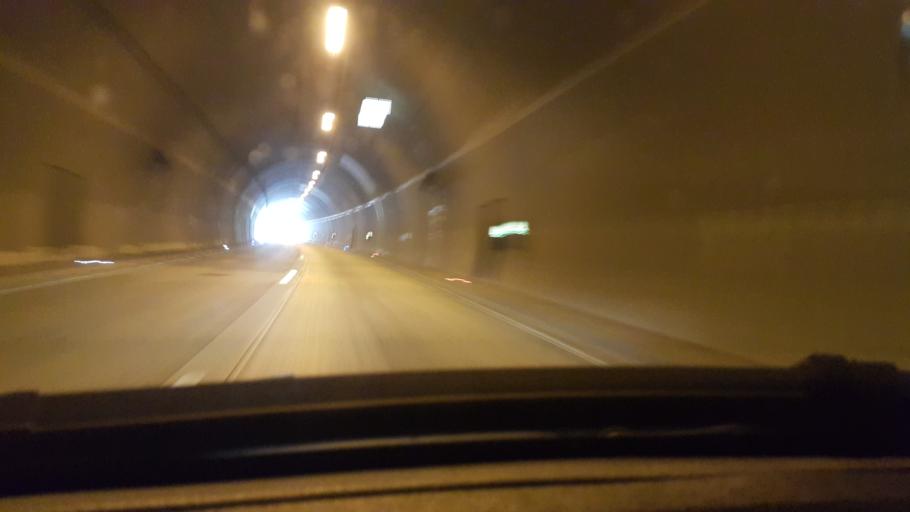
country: SI
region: Zagorje ob Savi
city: Izlake
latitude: 46.1819
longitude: 14.8470
